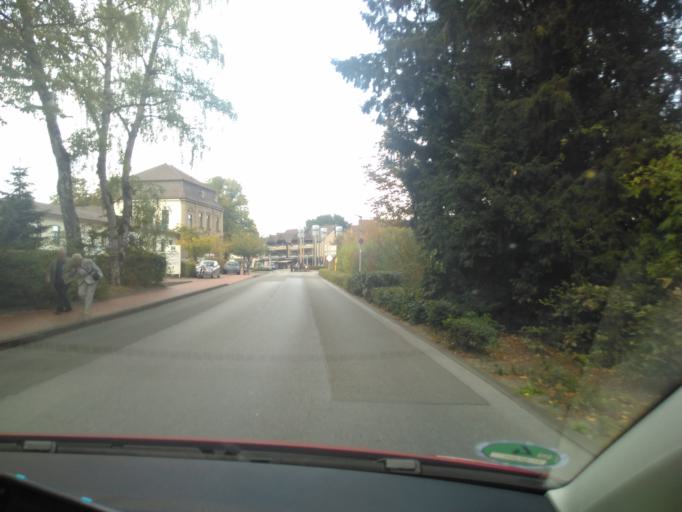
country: DE
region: Lower Saxony
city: Bad Rothenfelde
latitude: 52.1080
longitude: 8.1652
